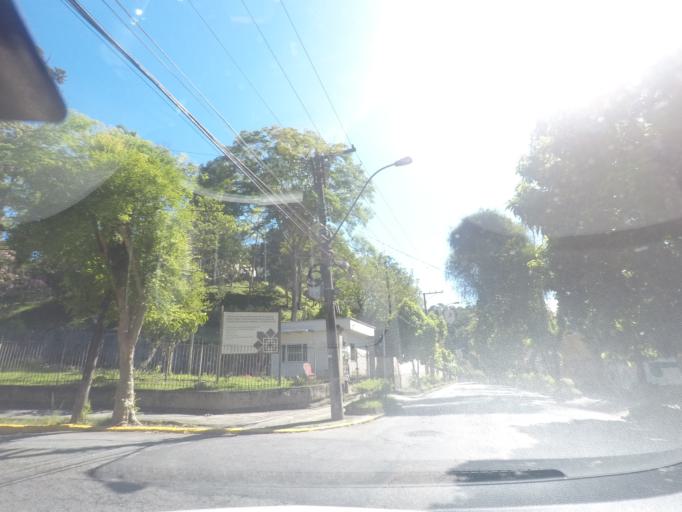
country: BR
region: Rio de Janeiro
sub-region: Petropolis
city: Petropolis
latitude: -22.5154
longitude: -43.1875
